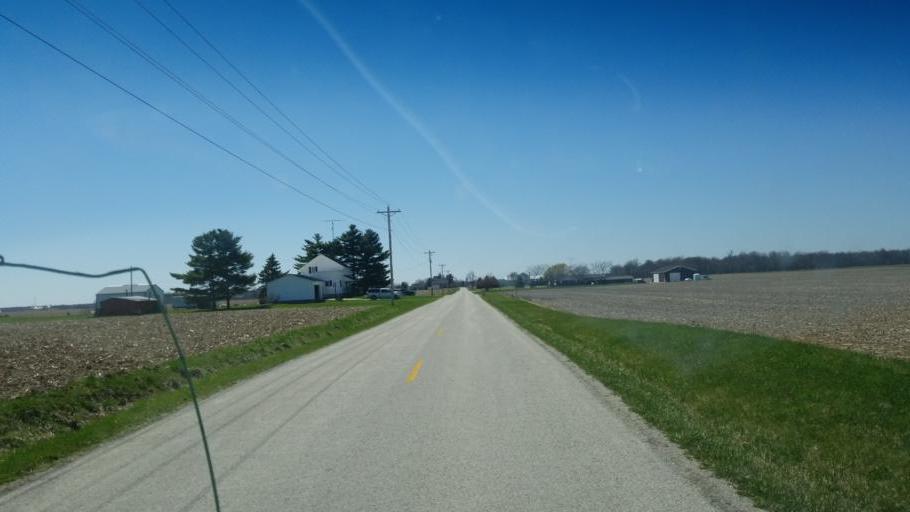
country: US
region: Ohio
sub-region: Crawford County
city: Bucyrus
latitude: 41.0228
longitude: -82.9441
